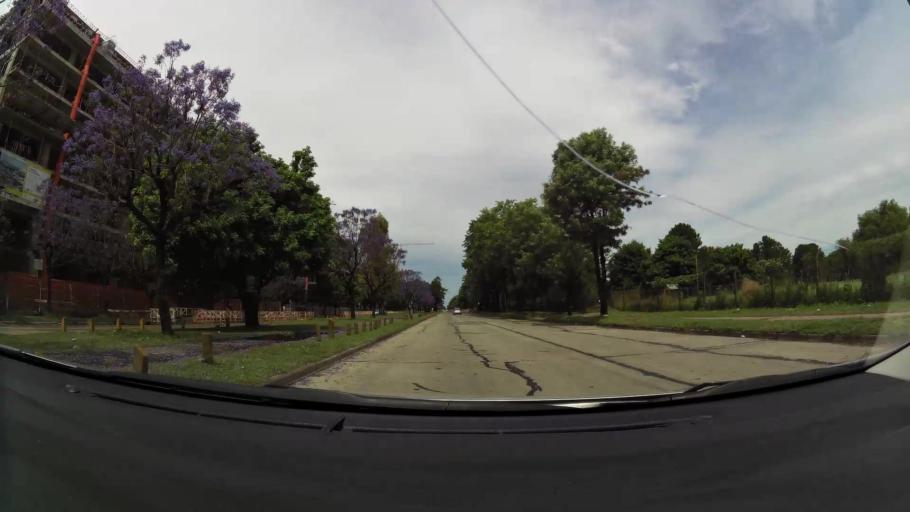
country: AR
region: Buenos Aires F.D.
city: Villa Lugano
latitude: -34.6762
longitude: -58.4554
